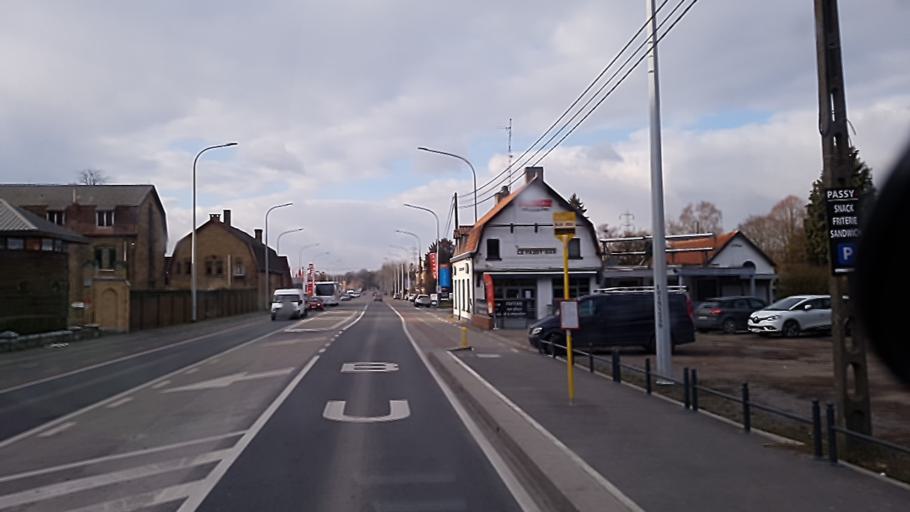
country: BE
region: Wallonia
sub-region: Province du Hainaut
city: Tournai
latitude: 50.6330
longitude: 3.3561
